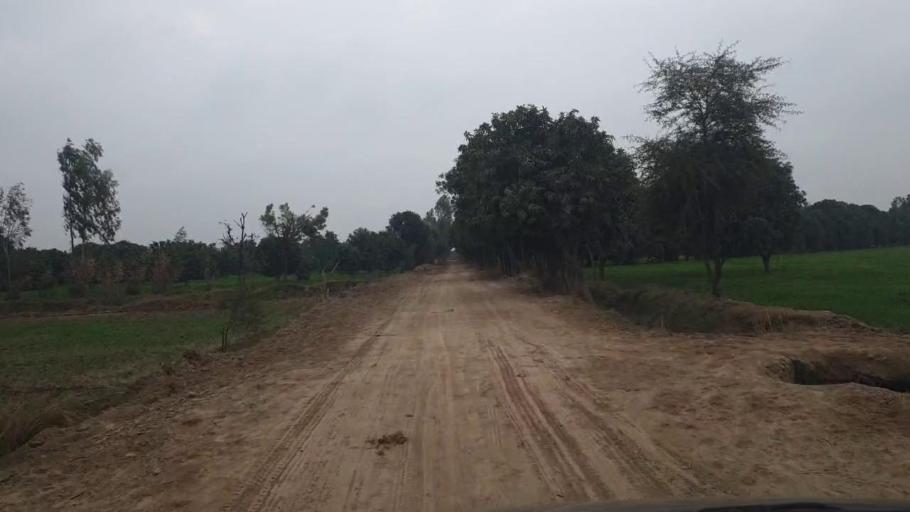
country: PK
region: Sindh
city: Shahdadpur
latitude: 25.8622
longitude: 68.6983
